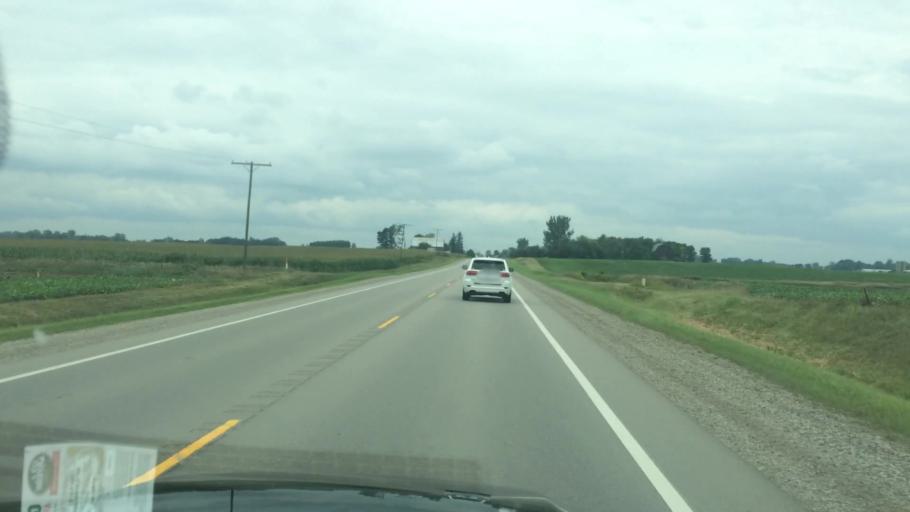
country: US
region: Michigan
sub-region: Sanilac County
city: Marlette
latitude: 43.4046
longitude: -83.0867
